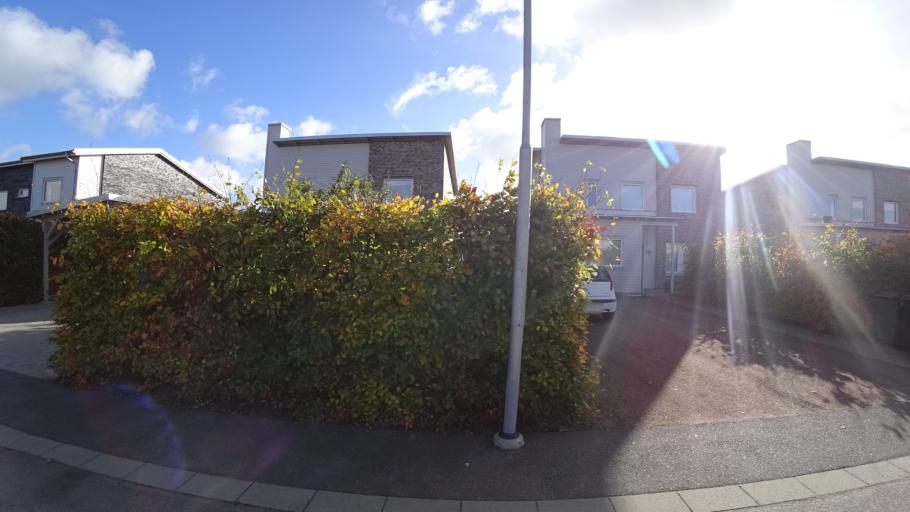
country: SE
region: Skane
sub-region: Staffanstorps Kommun
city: Hjaerup
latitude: 55.6719
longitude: 13.1518
